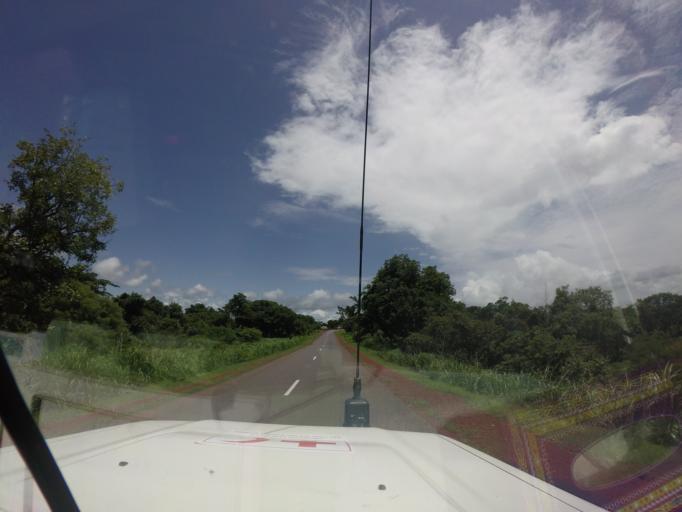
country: GN
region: Faranah
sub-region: Faranah Prefecture
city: Faranah
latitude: 10.0120
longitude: -10.8594
